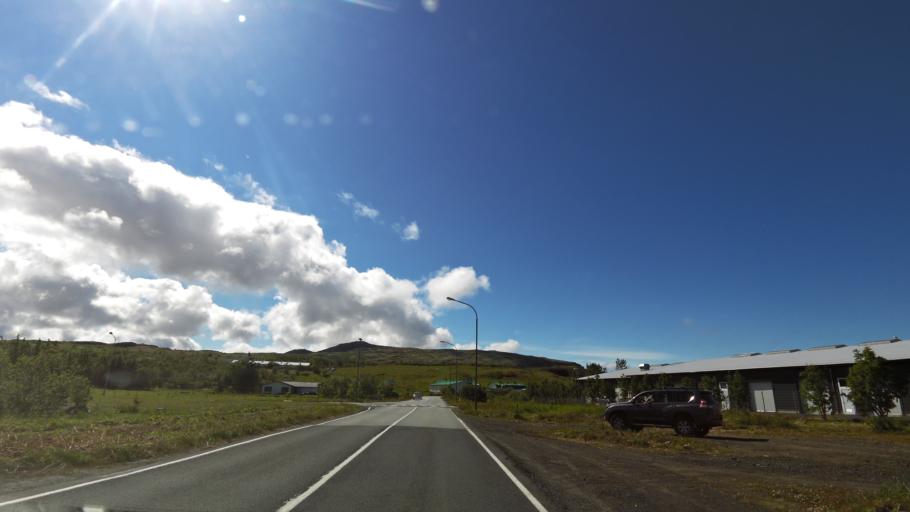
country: IS
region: Capital Region
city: Mosfellsbaer
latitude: 64.1611
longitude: -21.6757
